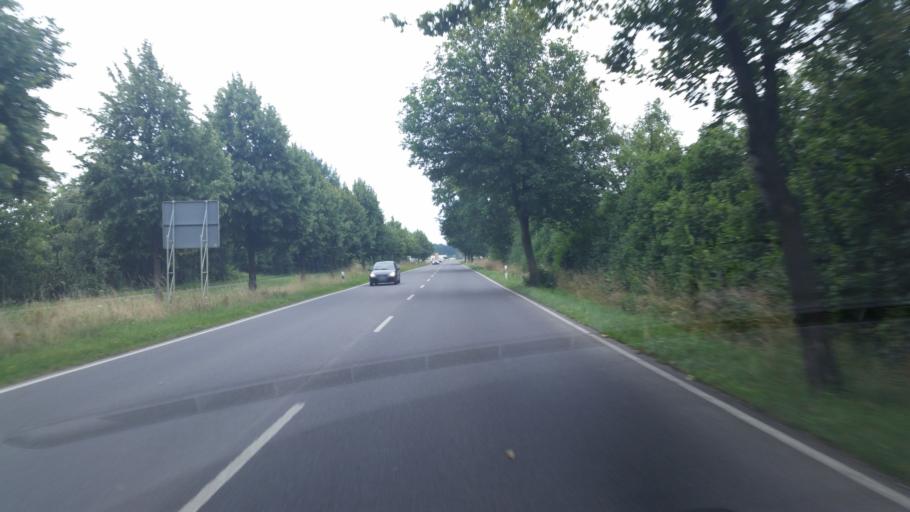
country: DE
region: Brandenburg
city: Senftenberg
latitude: 51.5034
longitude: 14.0635
